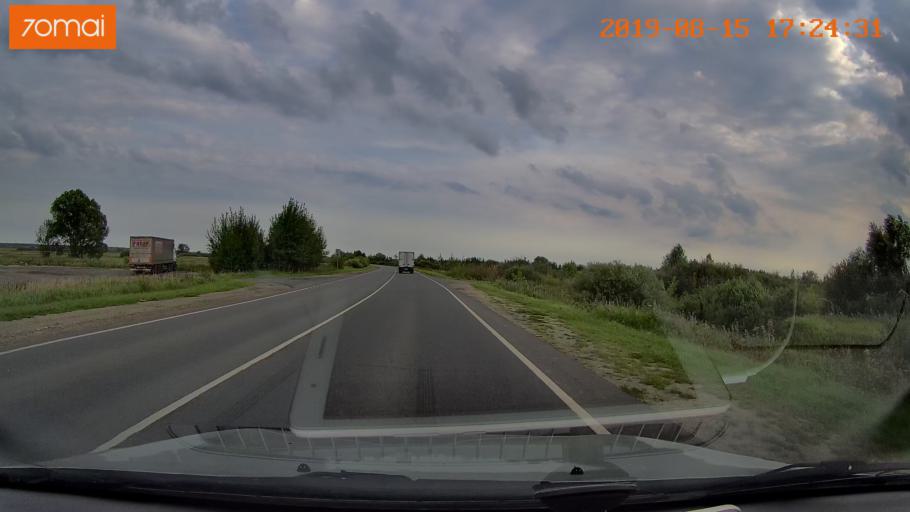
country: RU
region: Moskovskaya
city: Ashitkovo
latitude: 55.3859
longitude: 38.5556
